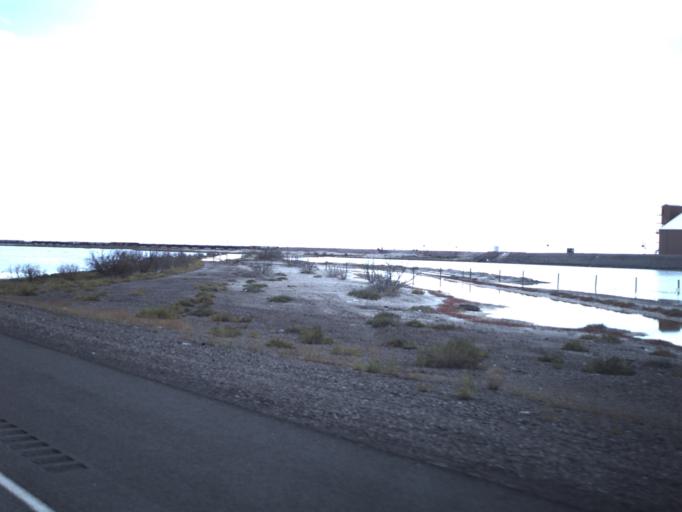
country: US
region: Utah
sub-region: Tooele County
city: Wendover
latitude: 40.7433
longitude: -113.9803
